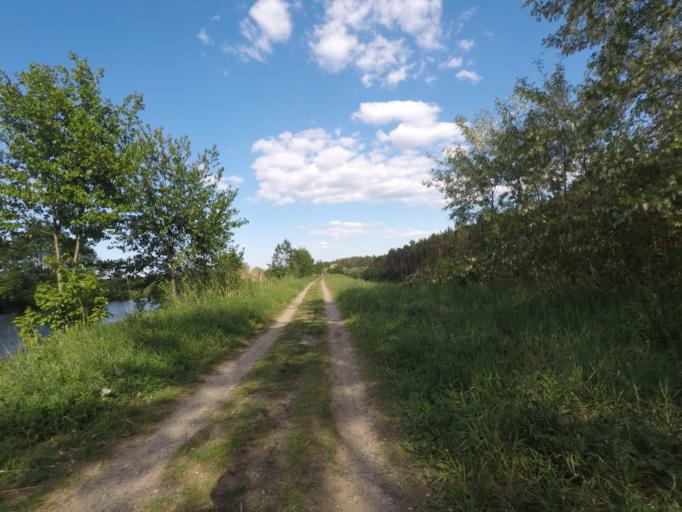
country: DE
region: Brandenburg
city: Eberswalde
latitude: 52.8528
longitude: 13.7997
